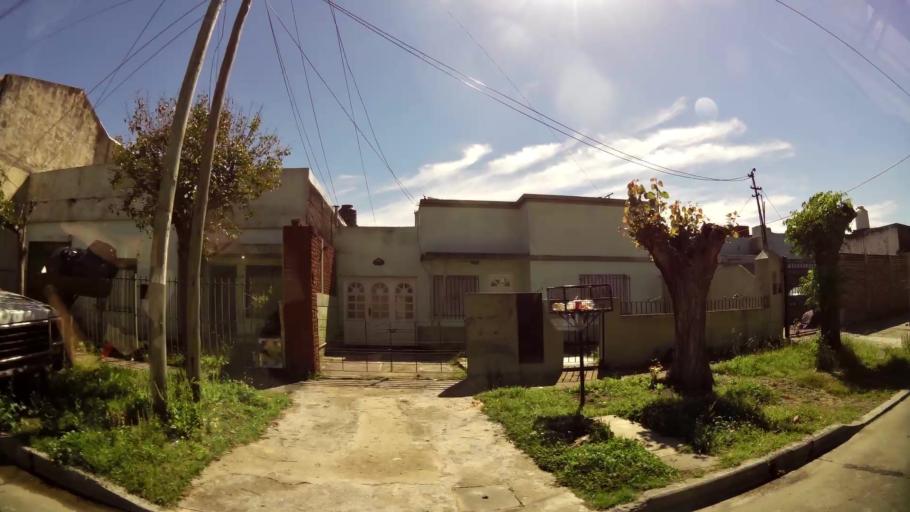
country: AR
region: Buenos Aires
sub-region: Partido de Avellaneda
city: Avellaneda
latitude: -34.6887
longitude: -58.3105
